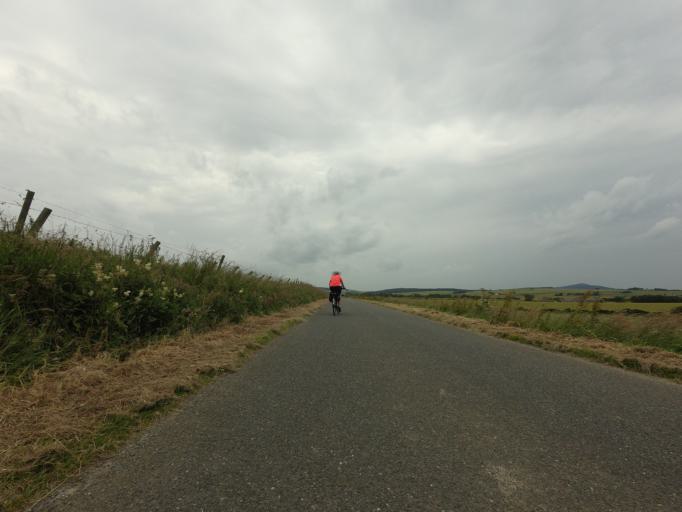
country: GB
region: Scotland
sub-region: Aberdeenshire
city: Portsoy
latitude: 57.6662
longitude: -2.7288
